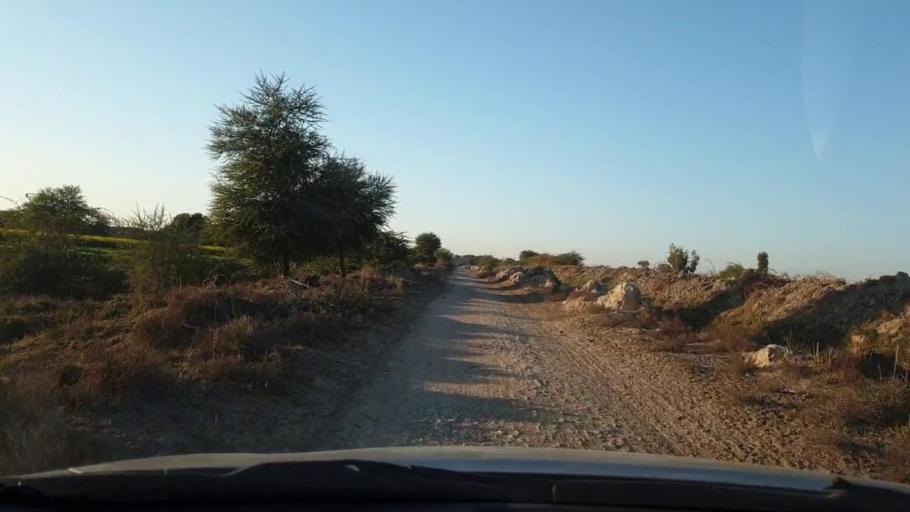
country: PK
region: Sindh
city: Jhol
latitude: 25.8931
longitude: 68.8909
